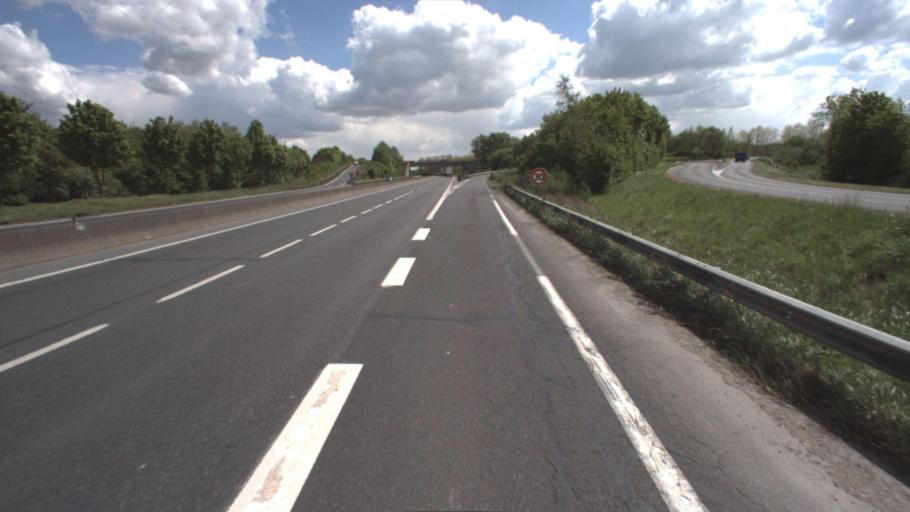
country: FR
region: Ile-de-France
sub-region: Departement de Seine-et-Marne
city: Tournan-en-Brie
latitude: 48.7349
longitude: 2.7746
